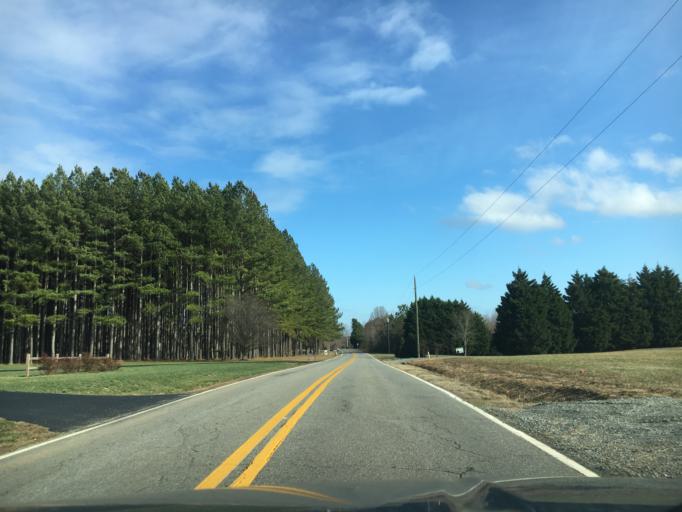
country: US
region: Virginia
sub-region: Halifax County
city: South Boston
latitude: 36.7348
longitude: -78.8773
